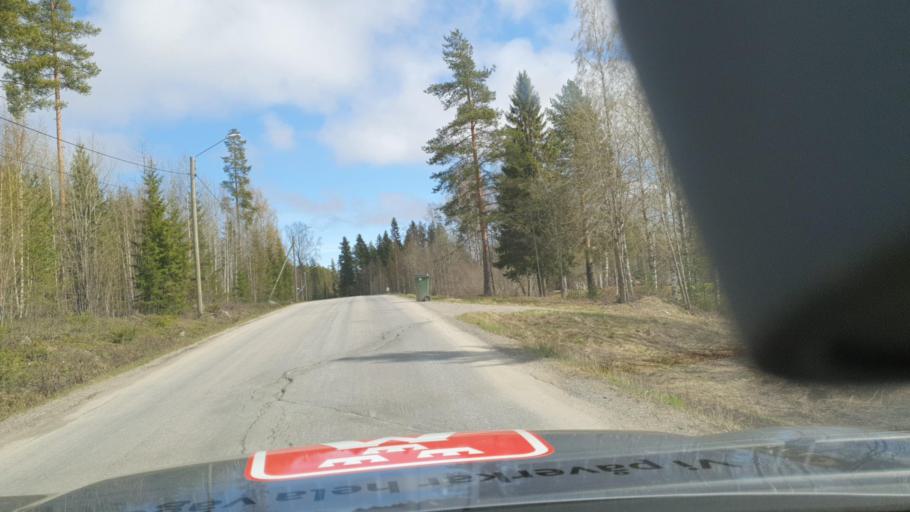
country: SE
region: Vaesterbotten
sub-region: Bjurholms Kommun
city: Bjurholm
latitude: 63.6956
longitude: 18.8875
